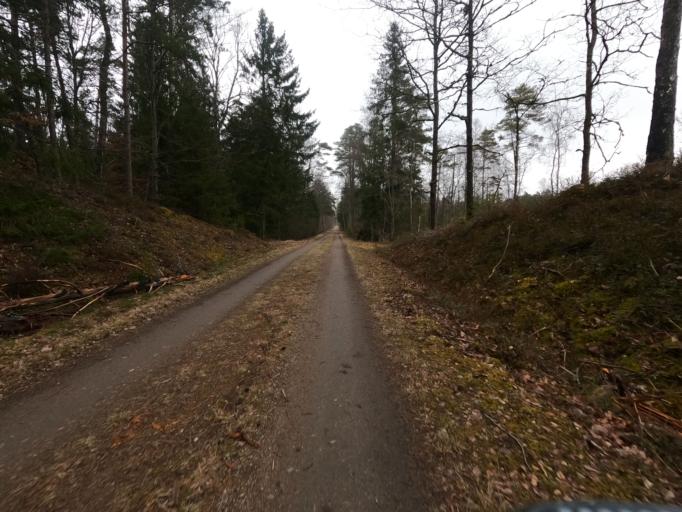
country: SE
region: Kronoberg
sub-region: Markaryds Kommun
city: Stromsnasbruk
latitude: 56.7934
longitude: 13.6672
